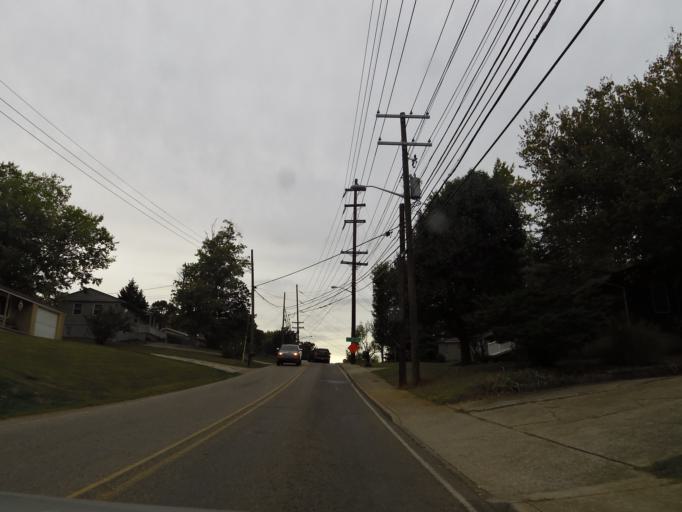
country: US
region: Tennessee
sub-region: Blount County
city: Louisville
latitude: 35.9102
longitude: -84.0249
